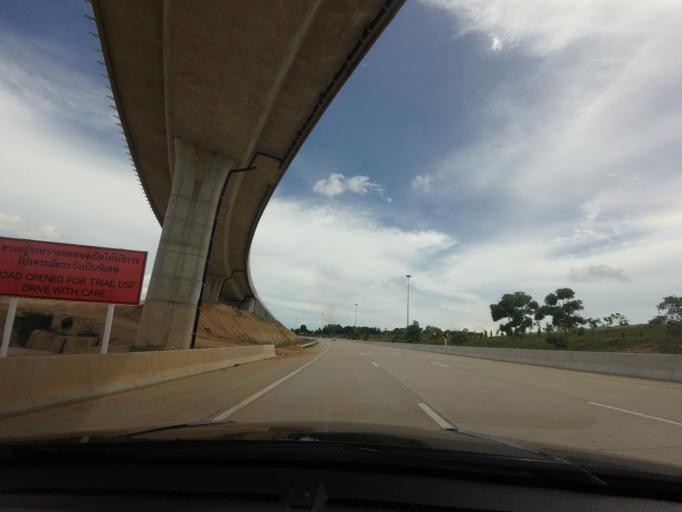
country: TH
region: Chon Buri
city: Phatthaya
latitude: 12.9490
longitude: 100.9583
